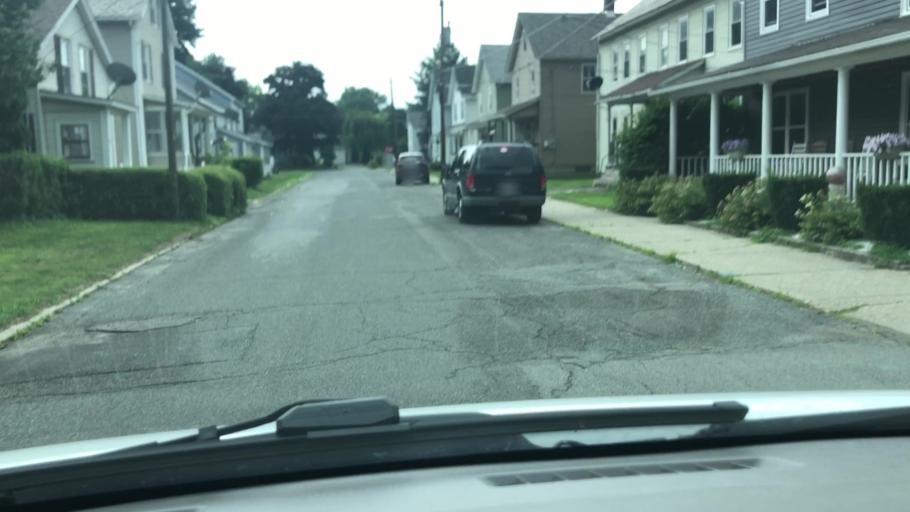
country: US
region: Massachusetts
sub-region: Berkshire County
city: Adams
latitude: 42.6296
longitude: -73.1131
